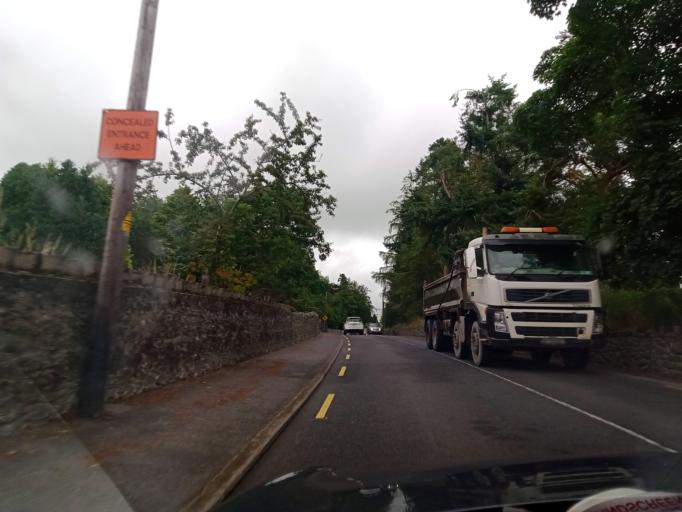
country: IE
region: Leinster
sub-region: Laois
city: Abbeyleix
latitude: 52.9118
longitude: -7.3396
